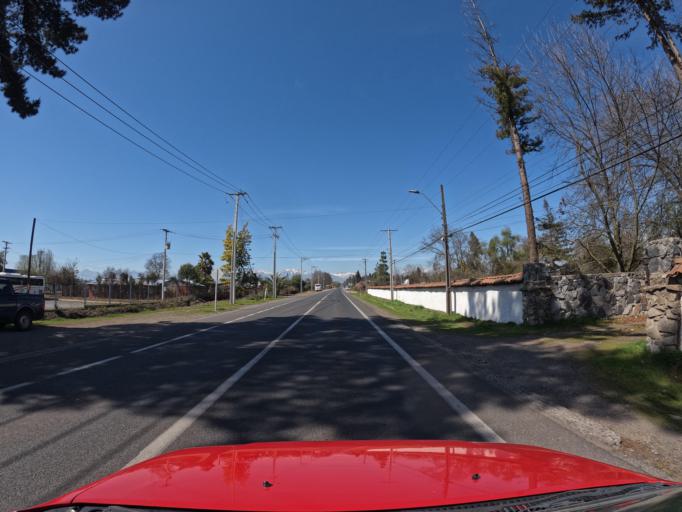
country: CL
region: Maule
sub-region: Provincia de Curico
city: Teno
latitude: -34.9615
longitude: -71.0929
